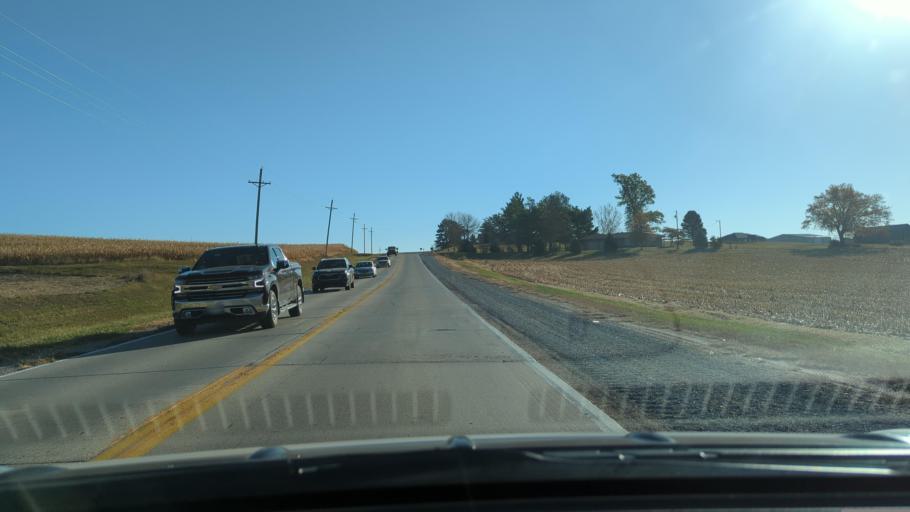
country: US
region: Nebraska
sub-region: Sarpy County
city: Papillion
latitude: 41.0925
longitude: -96.0343
